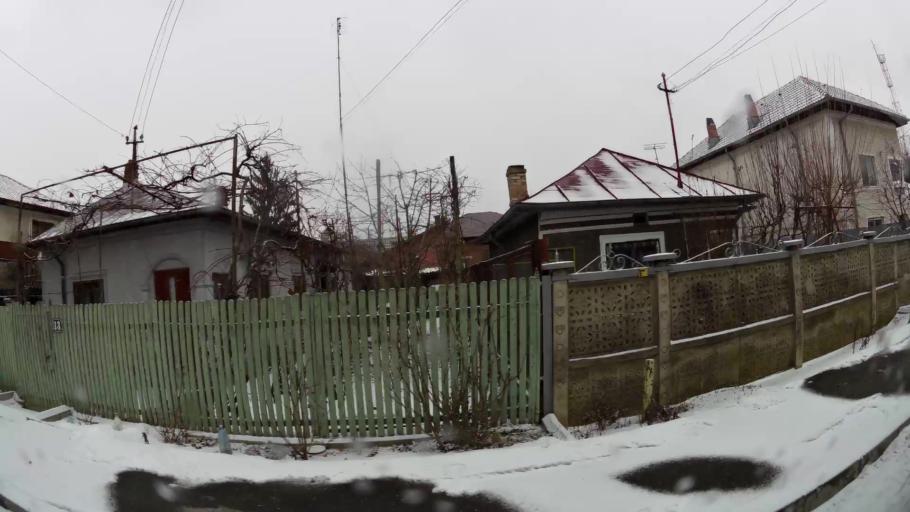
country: RO
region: Dambovita
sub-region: Municipiul Targoviste
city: Targoviste
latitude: 44.9159
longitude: 25.4634
